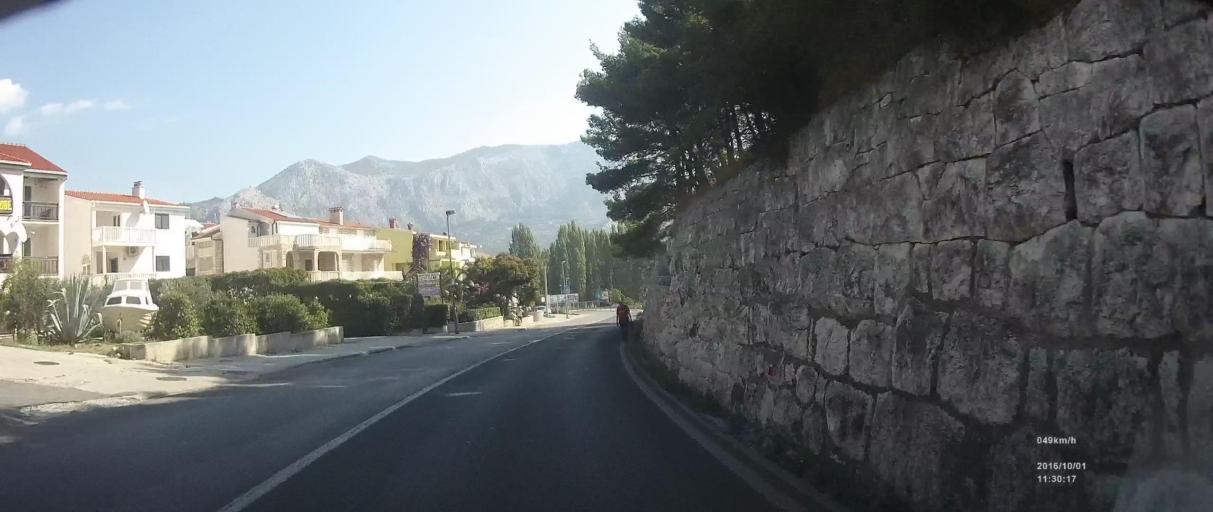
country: HR
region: Splitsko-Dalmatinska
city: Duce
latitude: 43.4402
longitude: 16.6749
